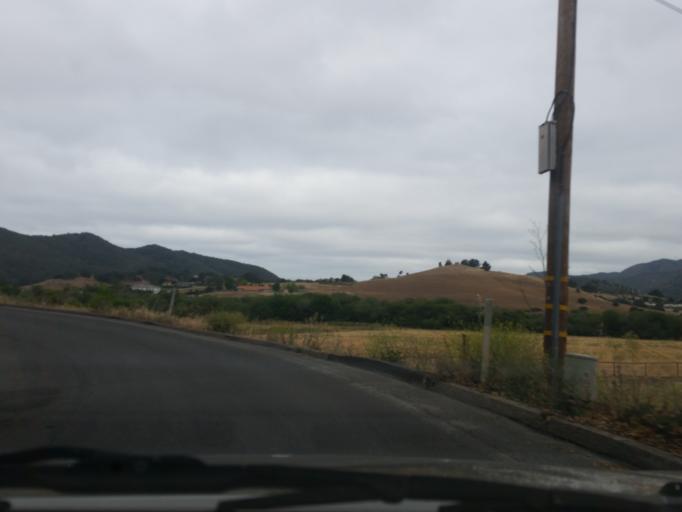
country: US
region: California
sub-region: San Luis Obispo County
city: Avila Beach
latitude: 35.1904
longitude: -120.6948
